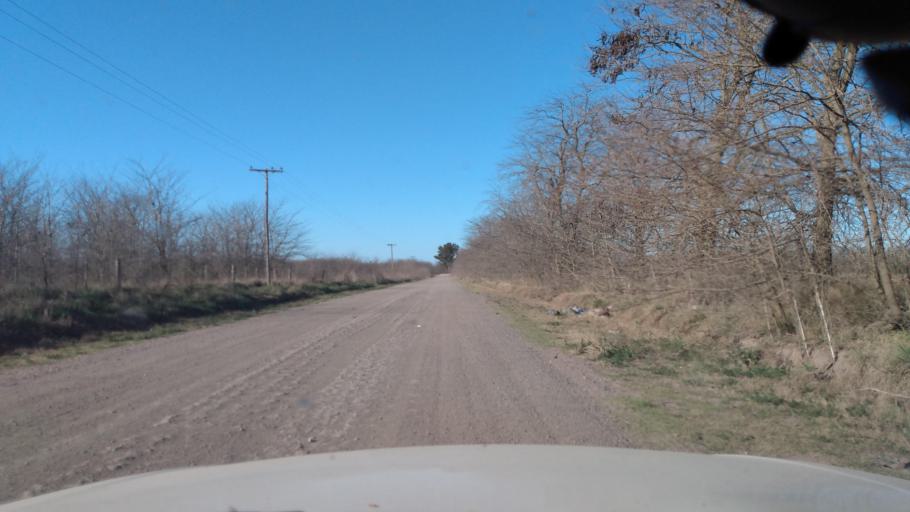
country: AR
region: Buenos Aires
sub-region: Partido de Mercedes
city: Mercedes
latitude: -34.6143
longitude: -59.3300
